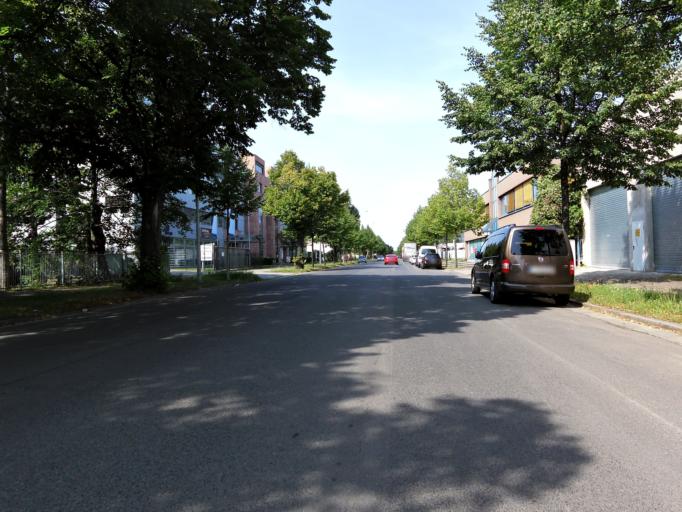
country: DE
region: Saxony
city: Leipzig
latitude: 51.3791
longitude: 12.3936
